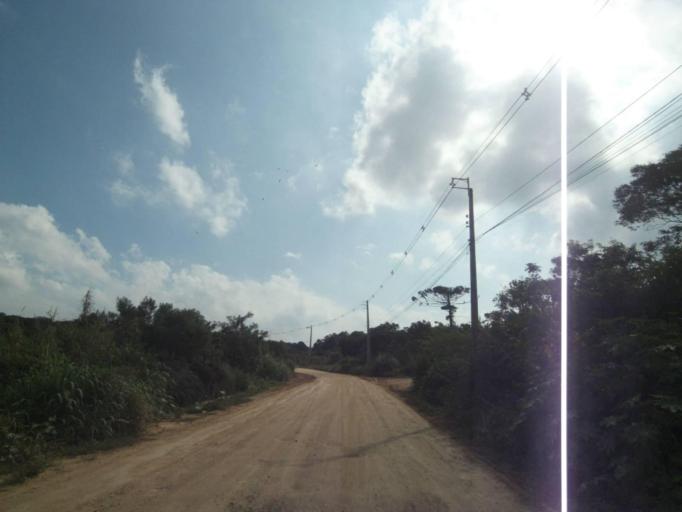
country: BR
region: Parana
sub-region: Araucaria
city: Araucaria
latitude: -25.5148
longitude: -49.3437
